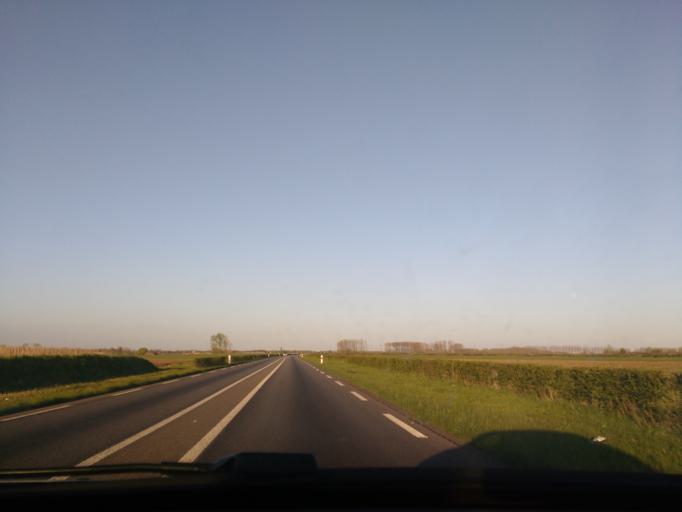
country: NL
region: Gelderland
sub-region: Gemeente Overbetuwe
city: Heteren
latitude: 51.9467
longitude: 5.7776
